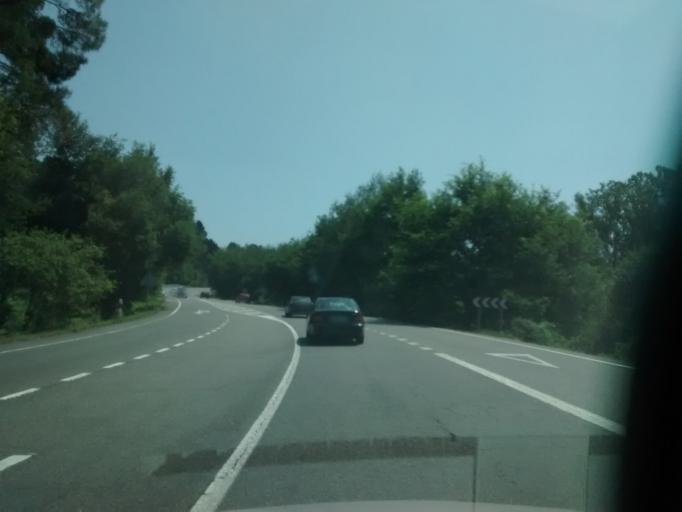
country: ES
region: Galicia
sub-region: Provincia de Ourense
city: O Carballino
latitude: 42.4252
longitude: -8.1064
